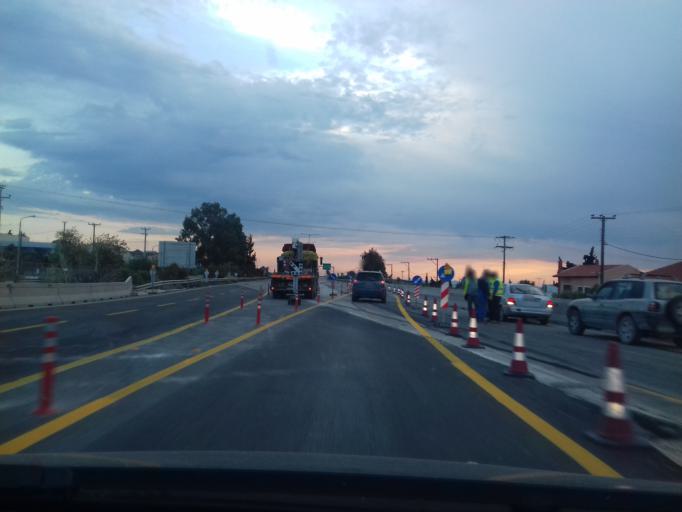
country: GR
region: West Greece
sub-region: Nomos Achaias
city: Rio
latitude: 38.2929
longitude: 21.7834
